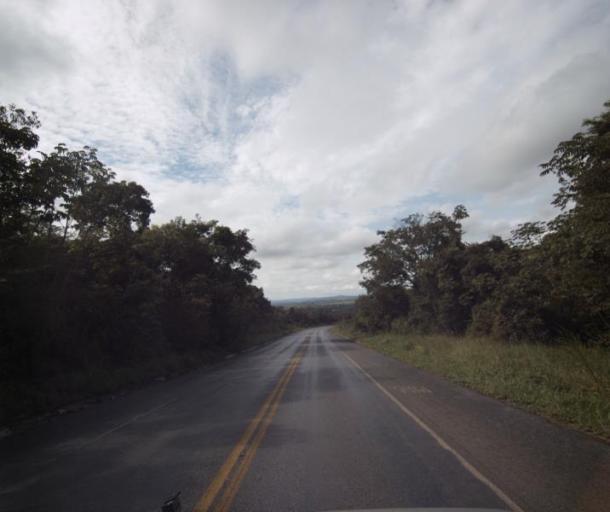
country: BR
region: Goias
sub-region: Pirenopolis
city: Pirenopolis
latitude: -15.5340
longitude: -48.6240
